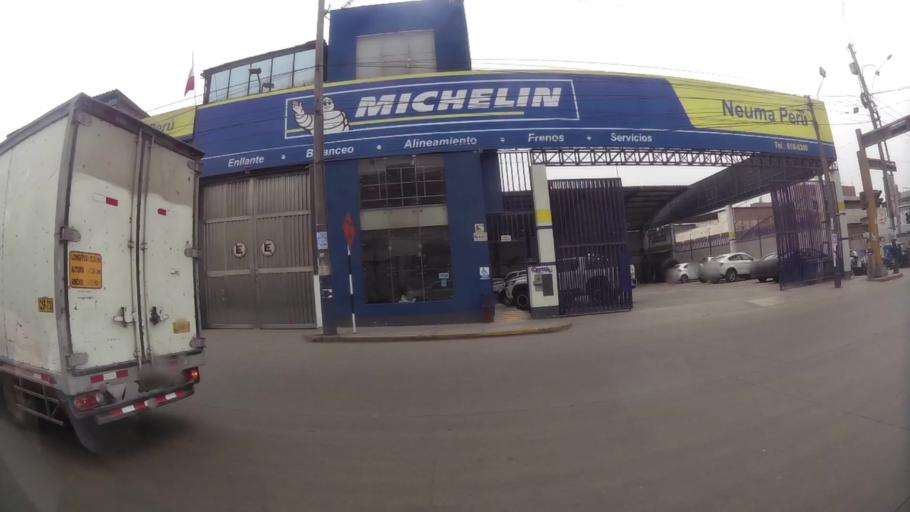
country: PE
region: Lima
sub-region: Lima
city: San Luis
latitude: -12.0633
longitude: -76.9824
